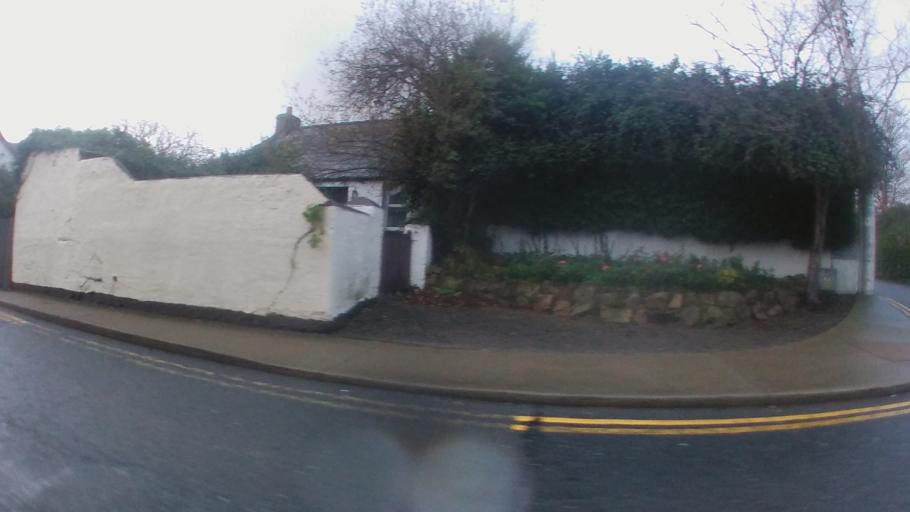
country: IE
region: Leinster
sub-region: Wicklow
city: Kilcoole
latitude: 53.1085
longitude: -6.0648
